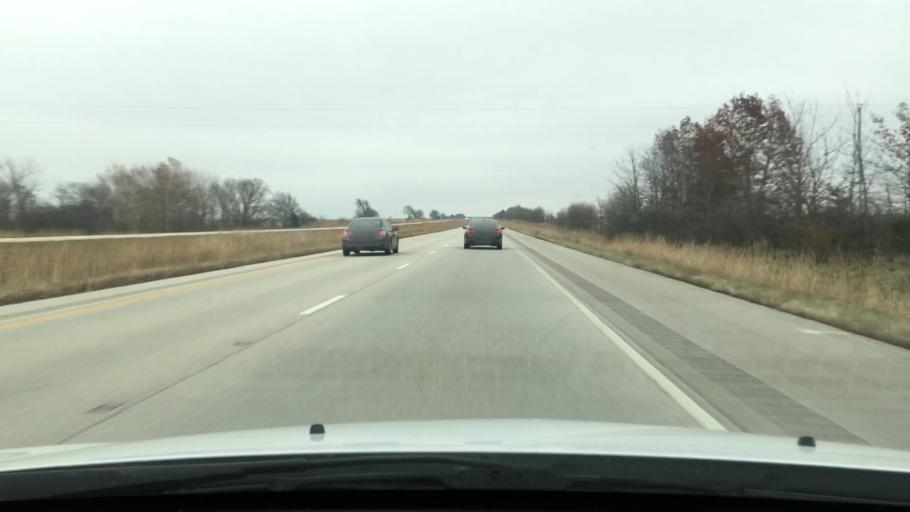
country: US
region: Illinois
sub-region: Sangamon County
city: New Berlin
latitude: 39.7407
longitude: -89.8732
